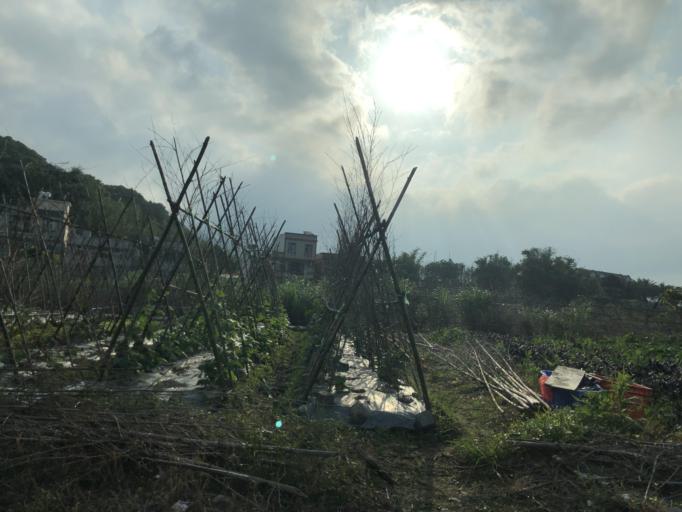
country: TW
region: Taiwan
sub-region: Keelung
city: Keelung
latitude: 25.2100
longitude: 121.6466
